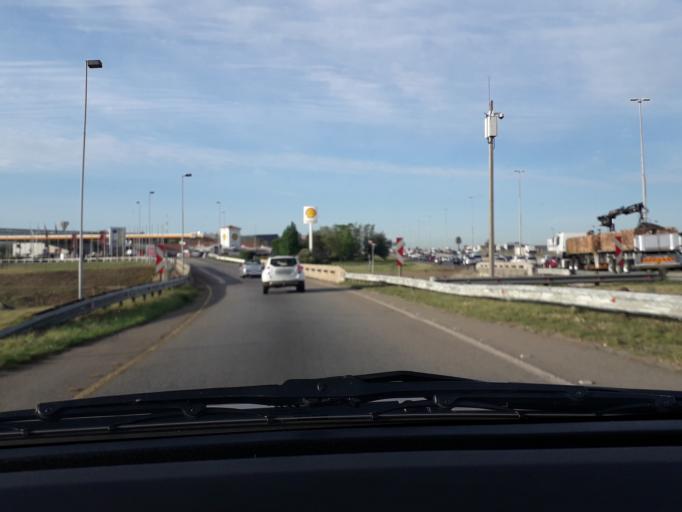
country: ZA
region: Gauteng
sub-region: City of Johannesburg Metropolitan Municipality
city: Midrand
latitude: -25.9281
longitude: 28.1459
